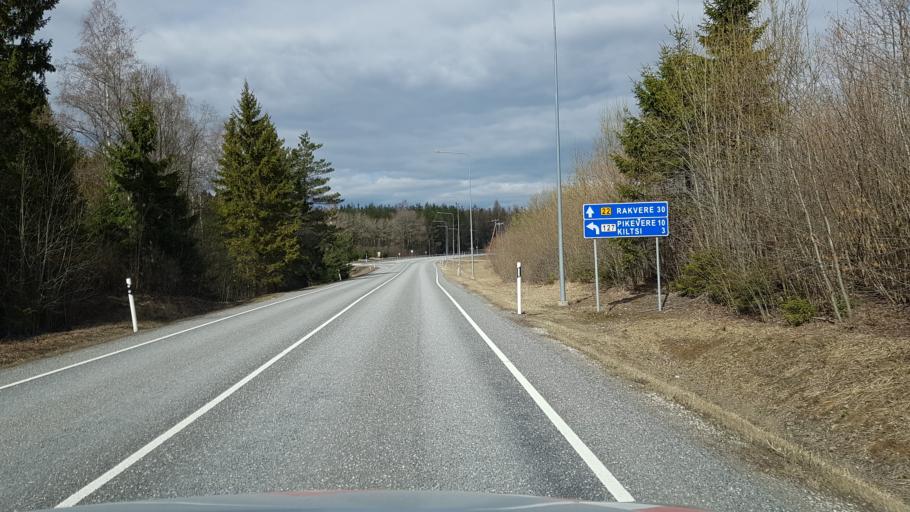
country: EE
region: Laeaene-Virumaa
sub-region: Vaeike-Maarja vald
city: Vaike-Maarja
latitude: 59.0975
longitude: 26.2282
